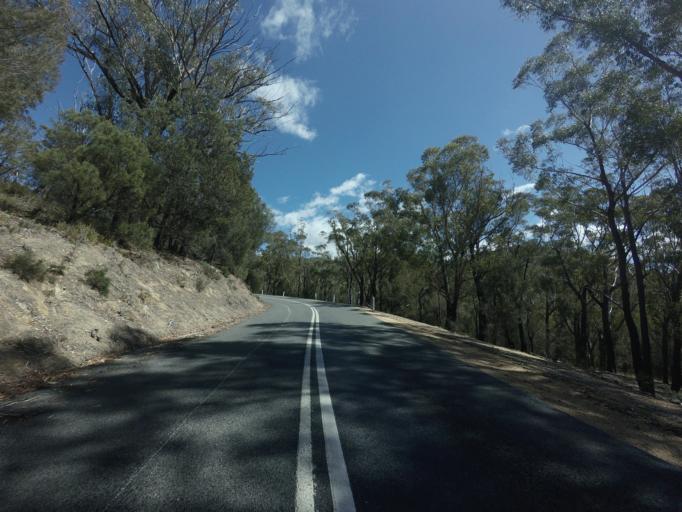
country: AU
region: Tasmania
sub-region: Break O'Day
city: St Helens
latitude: -41.6645
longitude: 148.2647
